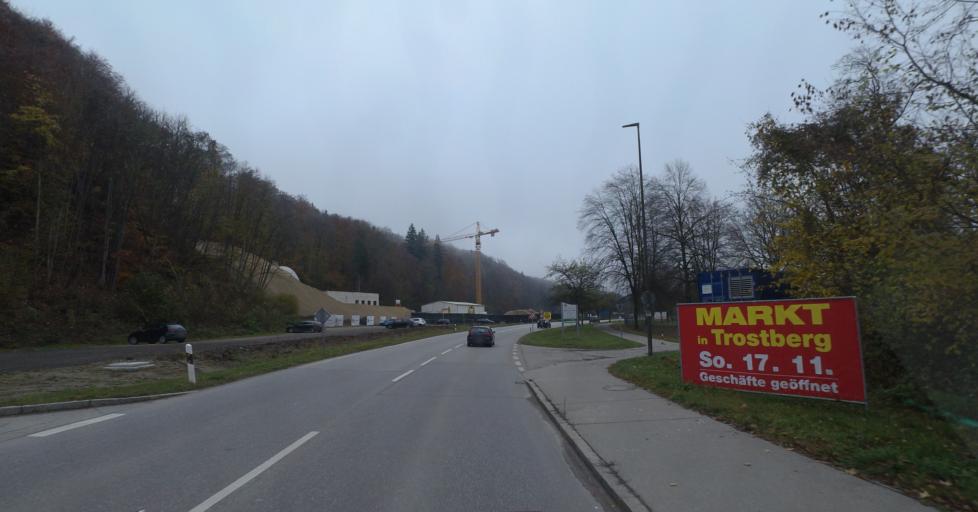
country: DE
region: Bavaria
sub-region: Upper Bavaria
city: Trostberg an der Alz
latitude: 48.0059
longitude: 12.5326
